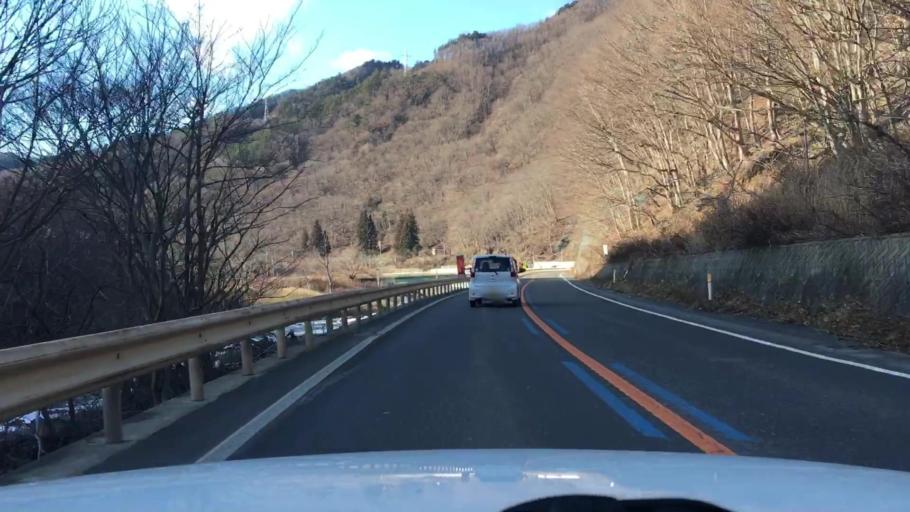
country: JP
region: Iwate
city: Miyako
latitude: 39.5993
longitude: 141.7365
